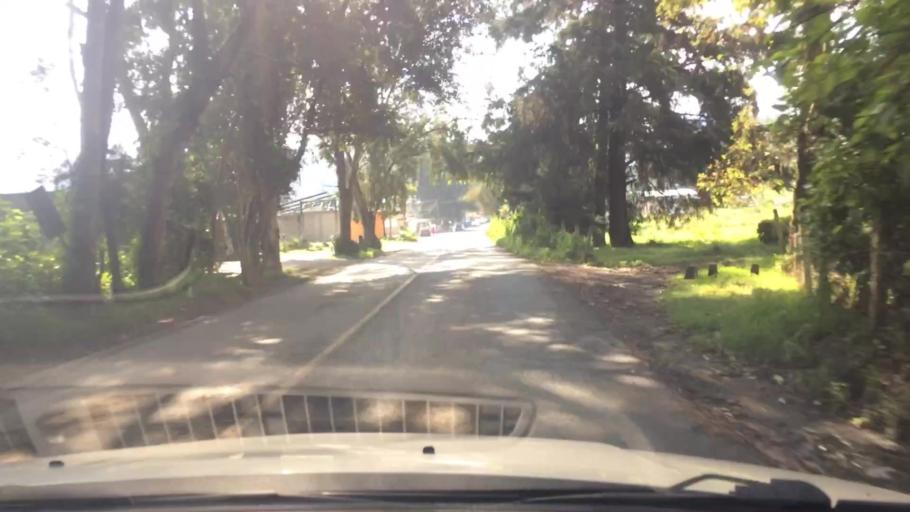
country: MX
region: Mexico
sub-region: Valle de Bravo
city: Cuadrilla de Dolores
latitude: 19.1487
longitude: -100.0728
